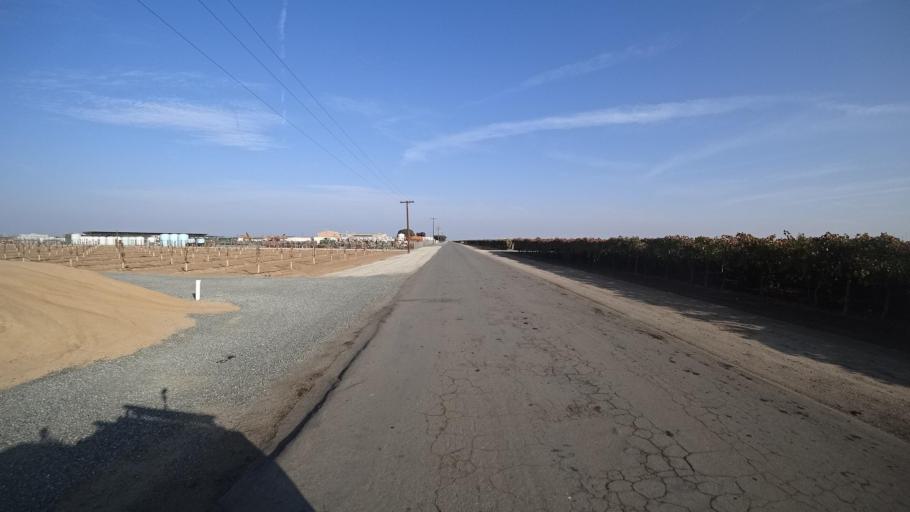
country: US
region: California
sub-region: Kern County
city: McFarland
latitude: 35.6958
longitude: -119.1871
